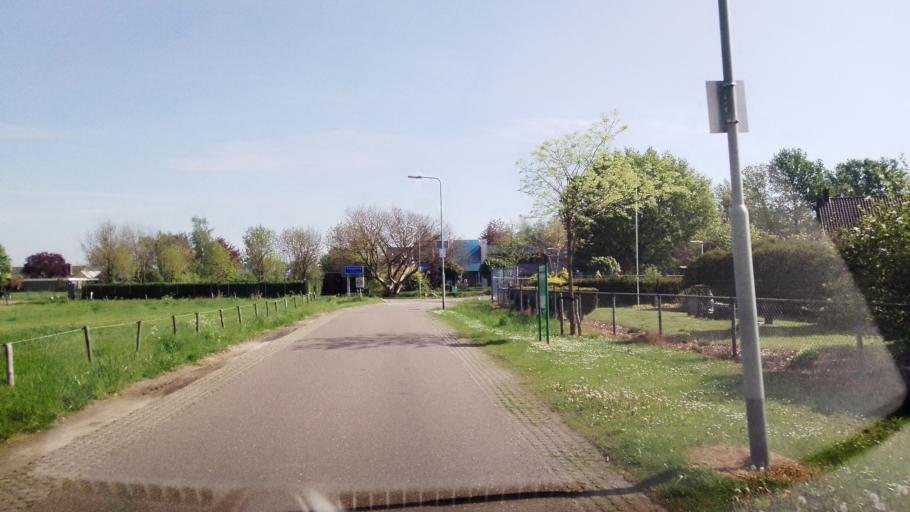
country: NL
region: Limburg
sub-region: Gemeente Peel en Maas
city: Maasbree
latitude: 51.4173
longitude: 6.0026
